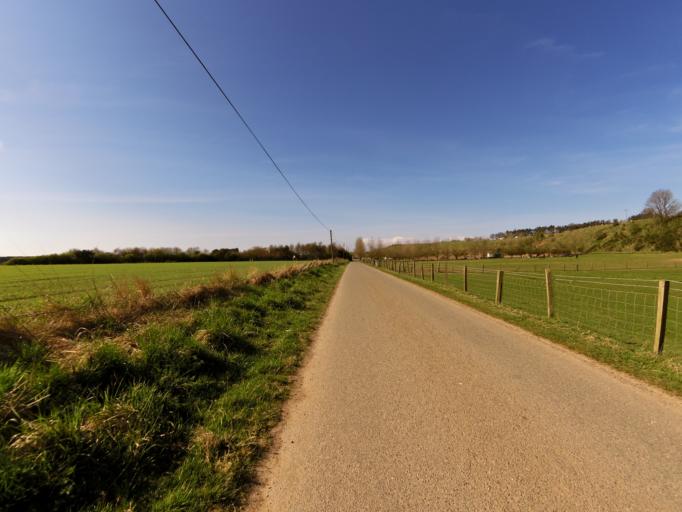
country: GB
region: Scotland
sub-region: Angus
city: Montrose
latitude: 56.7586
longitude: -2.4372
